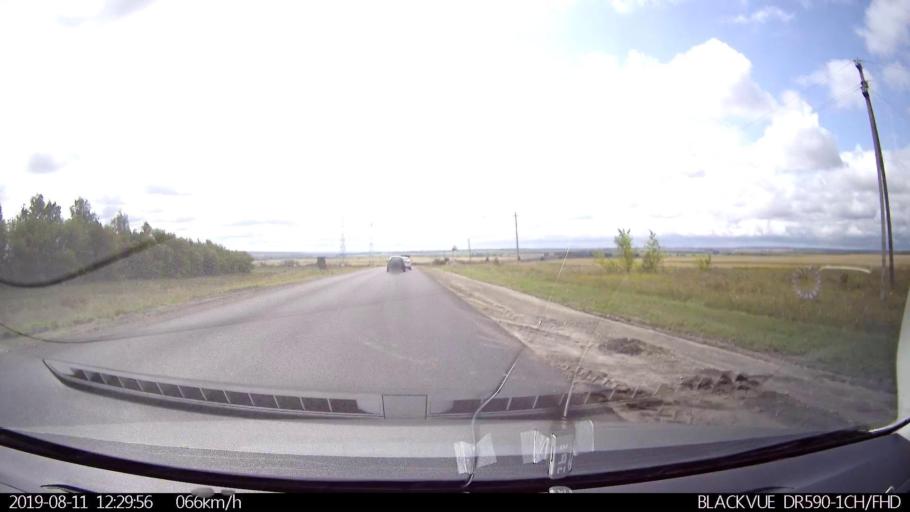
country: RU
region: Ulyanovsk
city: Ignatovka
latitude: 53.8301
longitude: 47.8982
